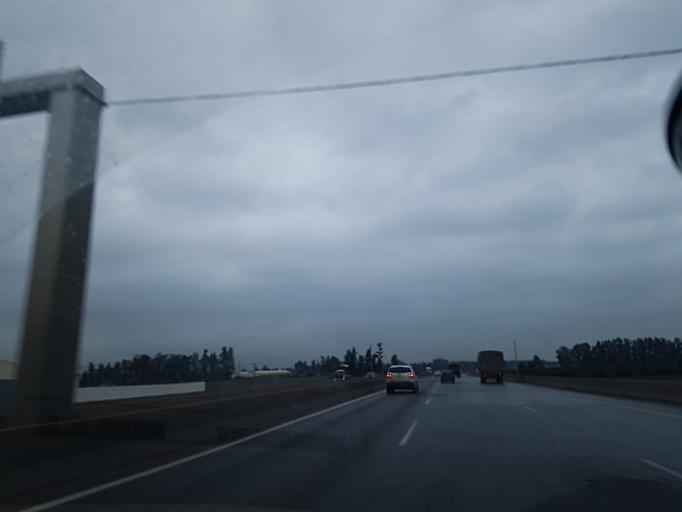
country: DZ
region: Boumerdes
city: Khemis el Khechna
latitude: 36.6648
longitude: 3.2819
